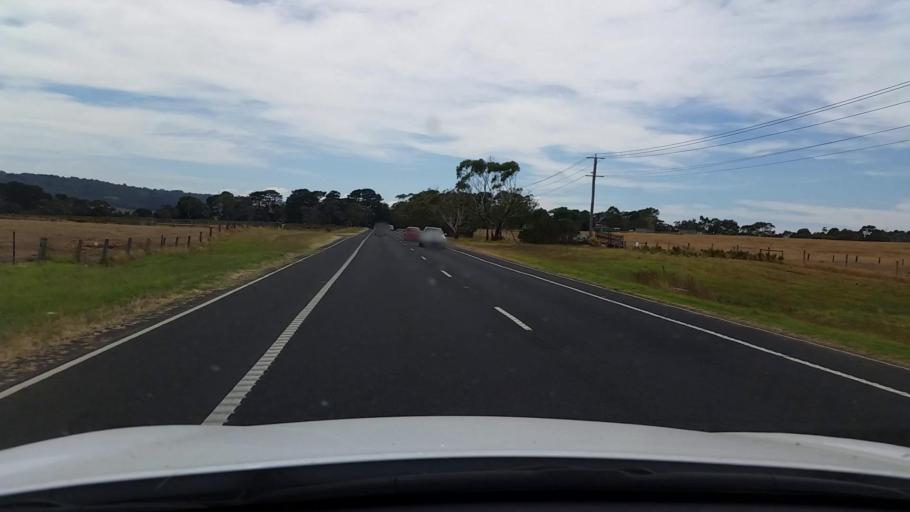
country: AU
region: Victoria
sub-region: Mornington Peninsula
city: Safety Beach
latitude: -38.3247
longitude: 145.0131
